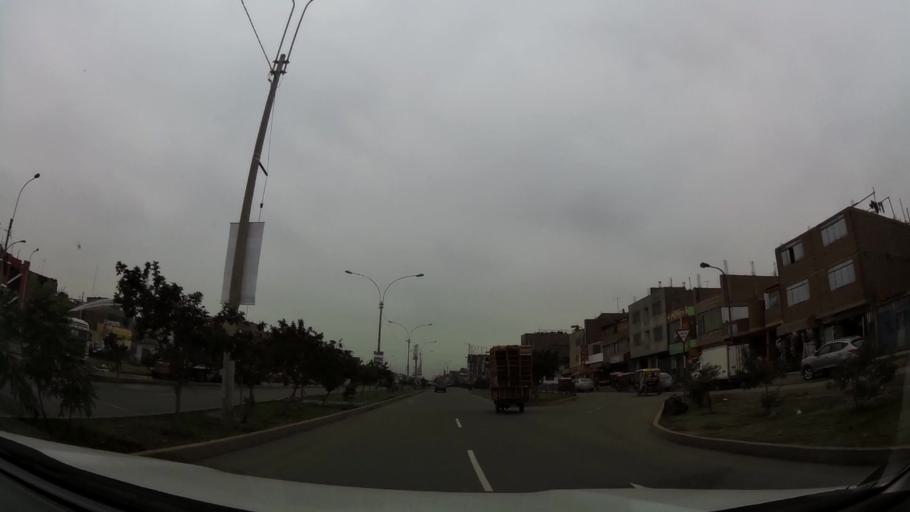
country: PE
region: Lima
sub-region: Lima
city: Vitarte
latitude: -12.0341
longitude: -76.9257
